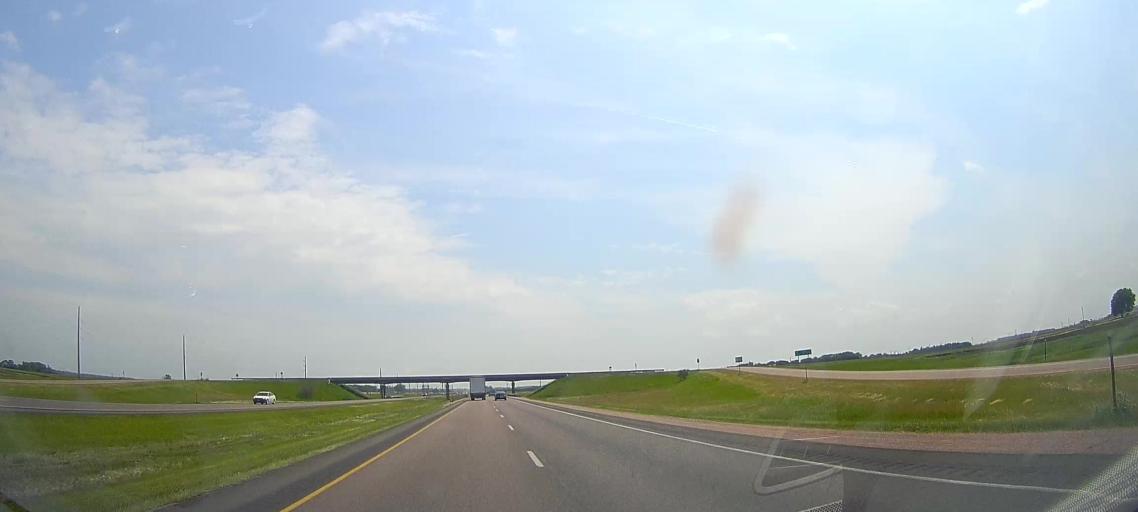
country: US
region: South Dakota
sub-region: Union County
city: Beresford
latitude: 43.1288
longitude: -96.7969
